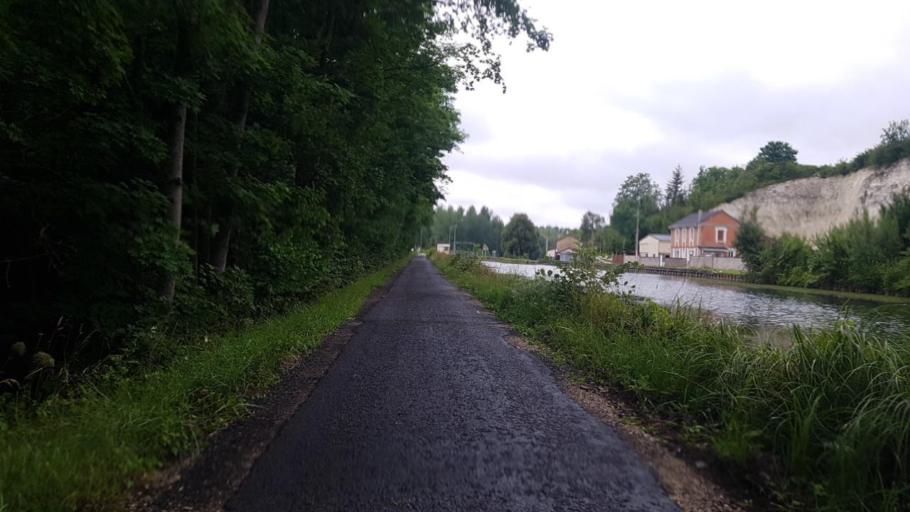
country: FR
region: Champagne-Ardenne
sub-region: Departement de la Marne
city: Vitry-le-Francois
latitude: 48.7480
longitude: 4.5744
